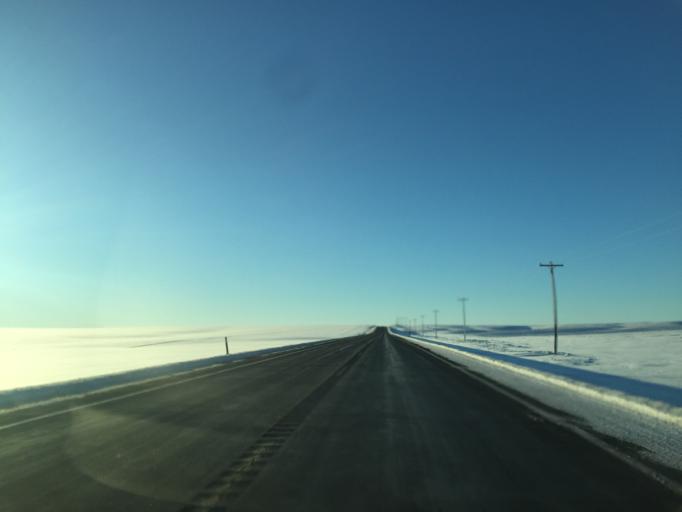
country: US
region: Washington
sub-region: Grant County
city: Soap Lake
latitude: 47.5996
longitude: -119.5473
